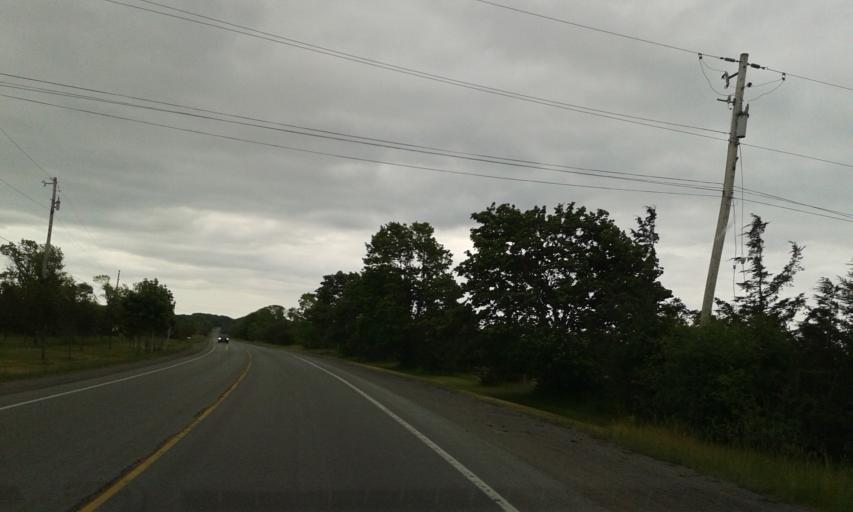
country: CA
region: Ontario
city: Quinte West
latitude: 43.9860
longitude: -77.5158
